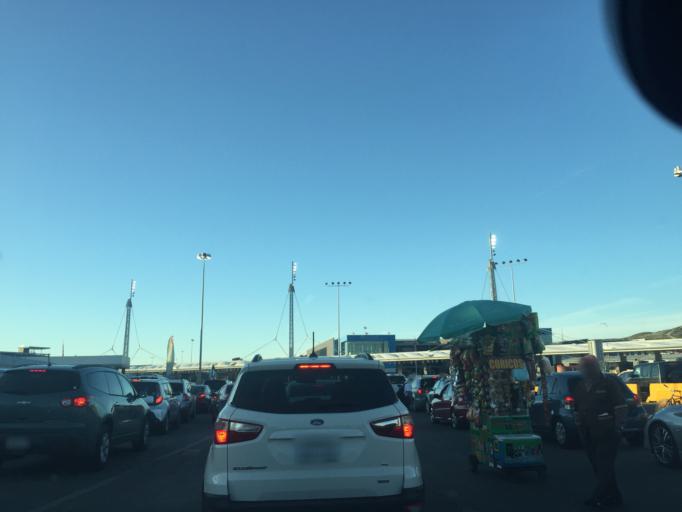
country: MX
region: Baja California
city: Tijuana
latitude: 32.5418
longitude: -117.0289
